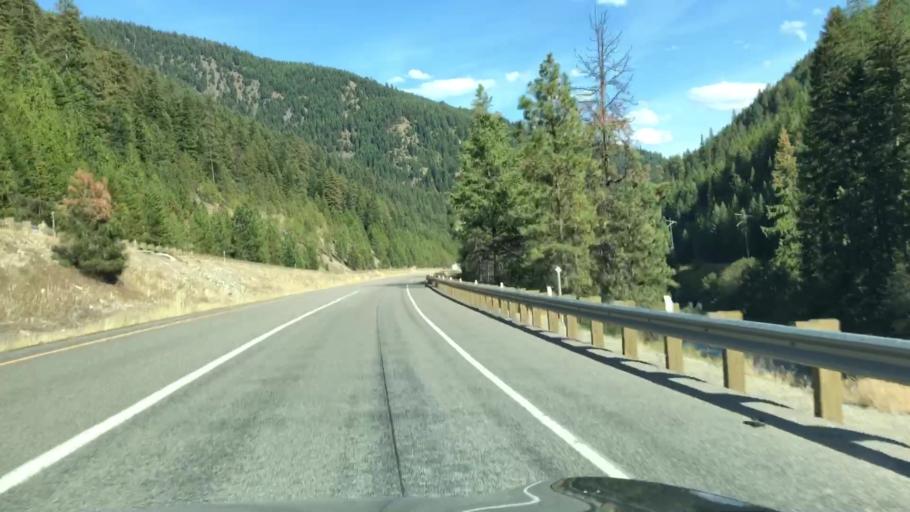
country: US
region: Montana
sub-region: Sanders County
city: Thompson Falls
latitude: 47.3137
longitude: -115.2260
